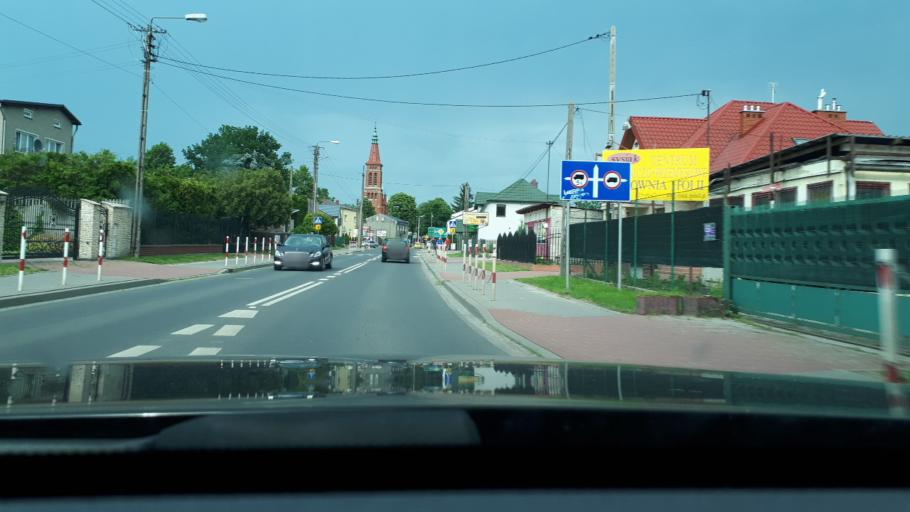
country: PL
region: Masovian Voivodeship
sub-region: Powiat warszawski zachodni
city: Leszno
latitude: 52.2578
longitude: 20.5875
